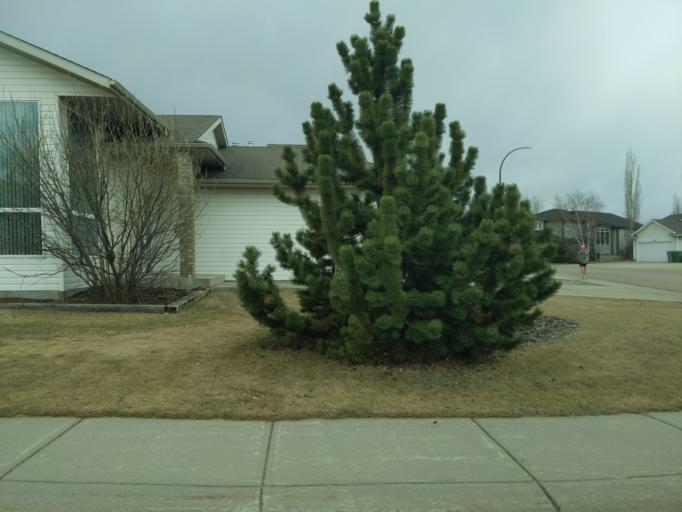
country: CA
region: Saskatchewan
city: Lloydminster
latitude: 53.2588
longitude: -110.0267
